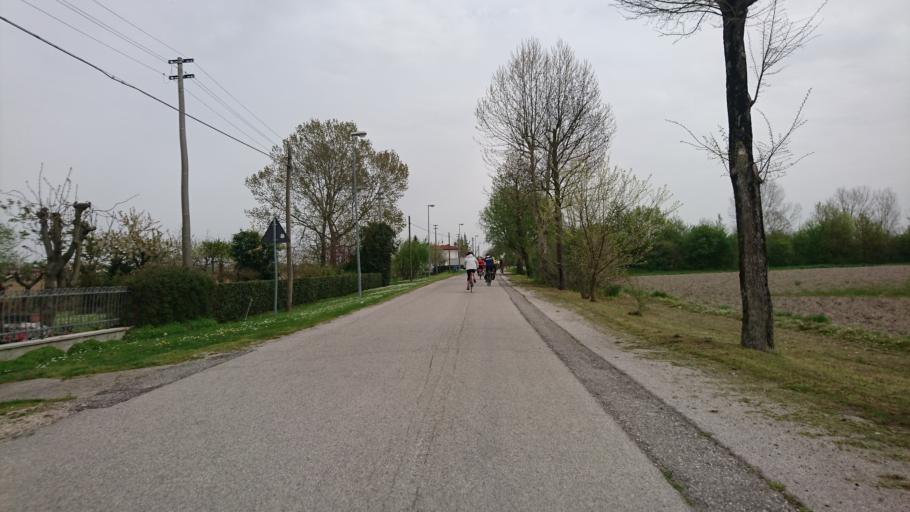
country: IT
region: Veneto
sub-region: Provincia di Venezia
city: Concordia Sagittaria
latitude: 45.7014
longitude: 12.8750
